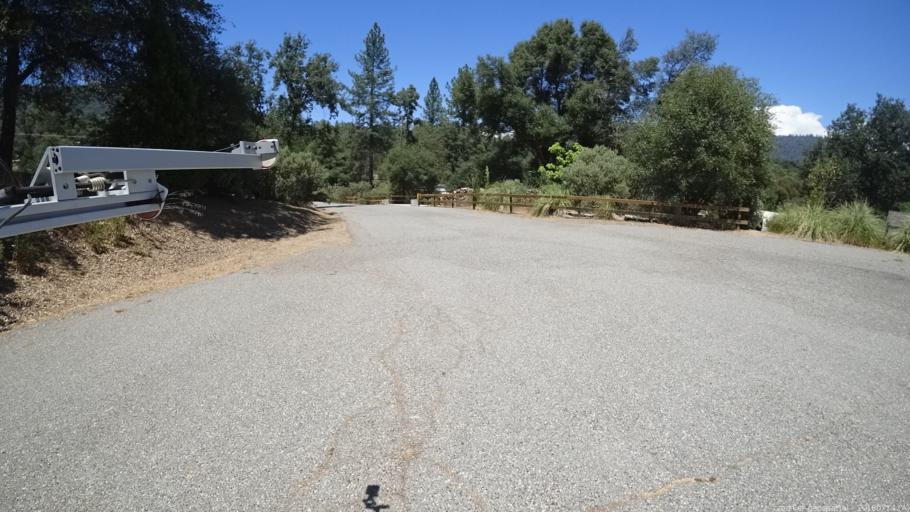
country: US
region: California
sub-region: Madera County
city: Ahwahnee
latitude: 37.4039
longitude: -119.7309
